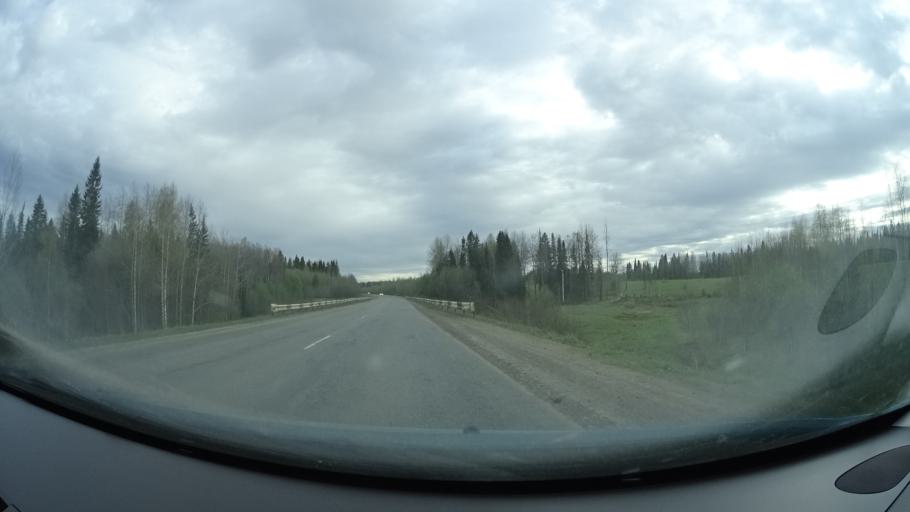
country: RU
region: Perm
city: Yugo-Kamskiy
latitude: 57.7709
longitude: 55.7502
